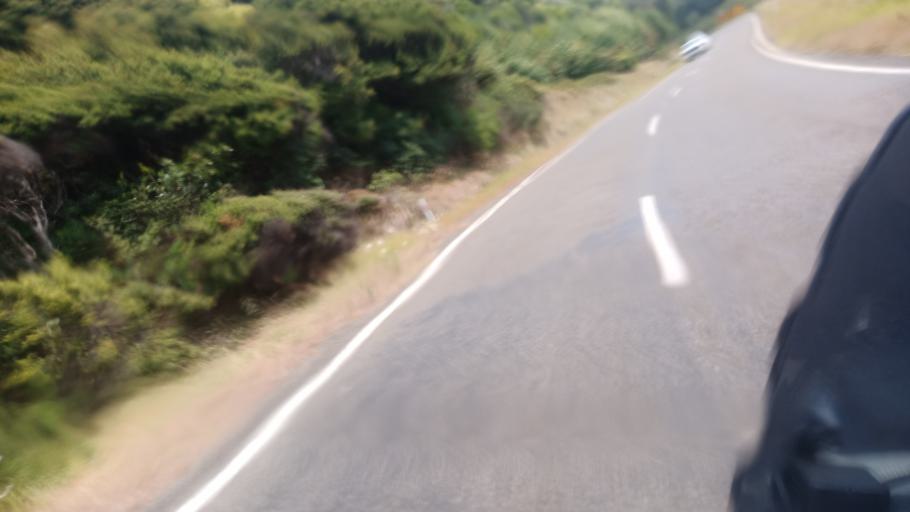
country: NZ
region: Bay of Plenty
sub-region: Opotiki District
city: Opotiki
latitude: -37.5902
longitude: 177.9816
